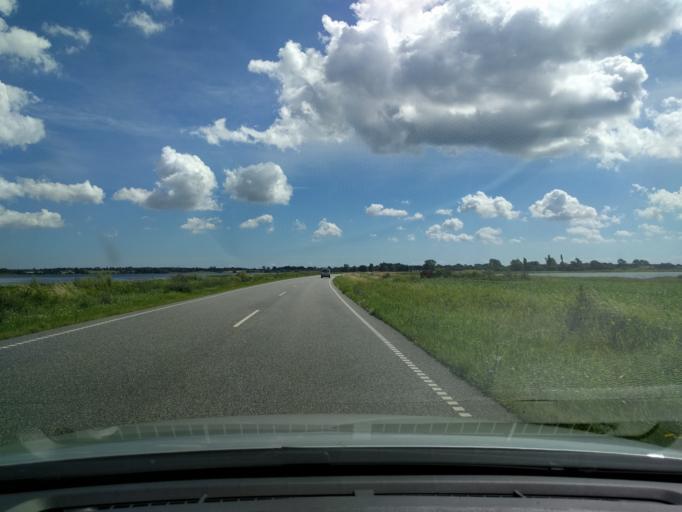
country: DK
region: Zealand
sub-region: Vordingborg Kommune
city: Nyrad
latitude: 54.9453
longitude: 11.9952
